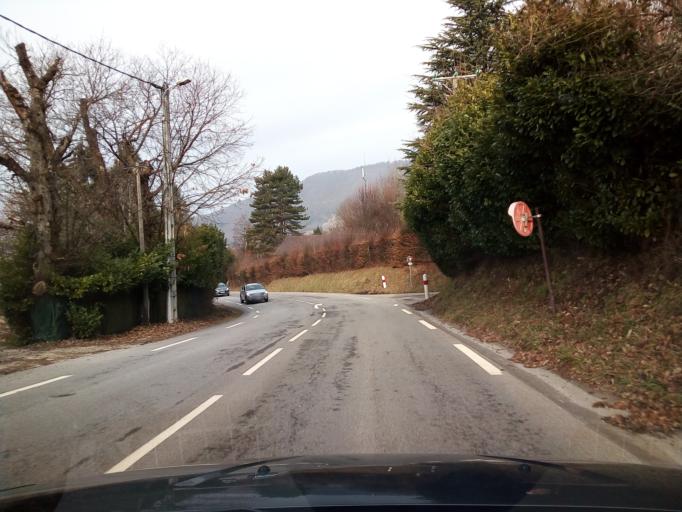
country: FR
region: Rhone-Alpes
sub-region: Departement de l'Isere
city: Revel
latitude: 45.1531
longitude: 5.8414
